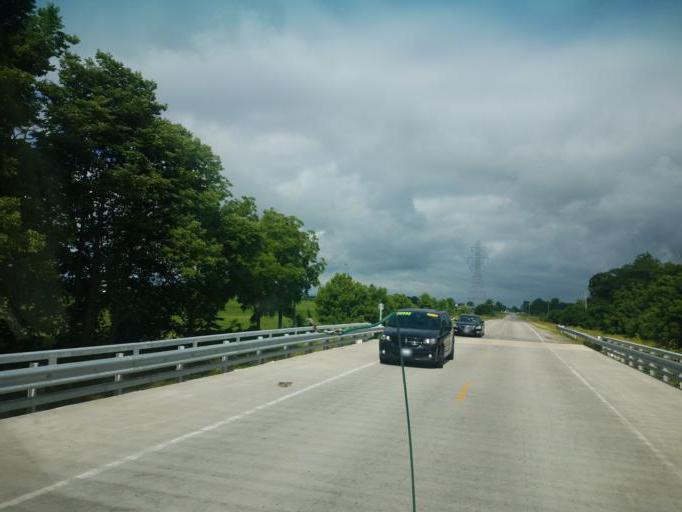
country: US
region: Ohio
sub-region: Union County
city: Richwood
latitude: 40.4019
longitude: -83.4162
